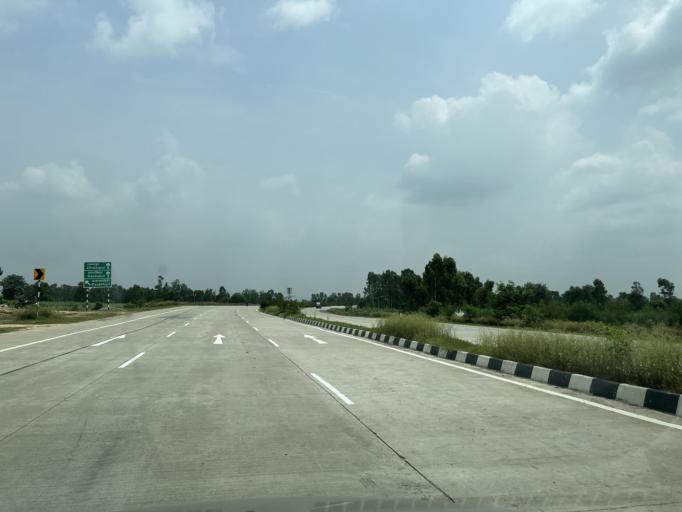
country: IN
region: Uttar Pradesh
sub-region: Bijnor
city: Nagina
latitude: 29.4310
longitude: 78.4113
